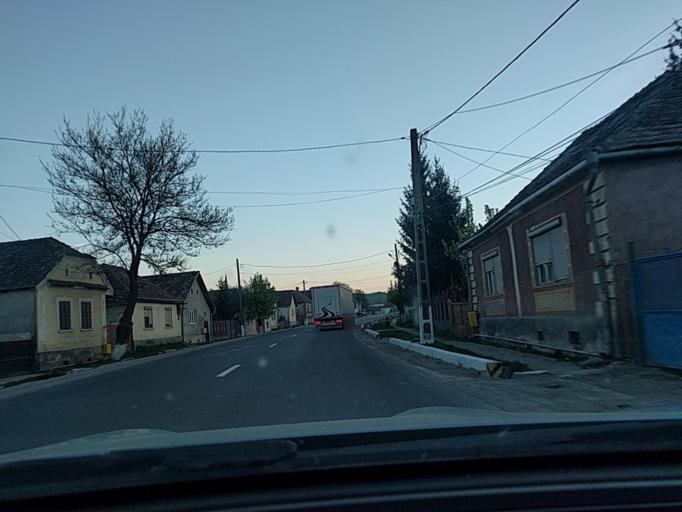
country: RO
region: Mures
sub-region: Comuna Balauseri
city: Chendu
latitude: 46.3584
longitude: 24.7185
